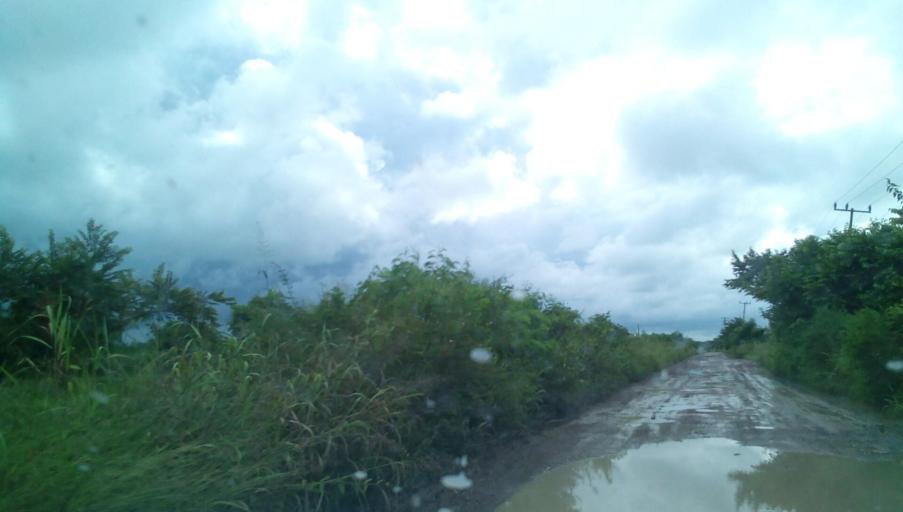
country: MX
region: Veracruz
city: Panuco
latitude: 21.8492
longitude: -98.1412
